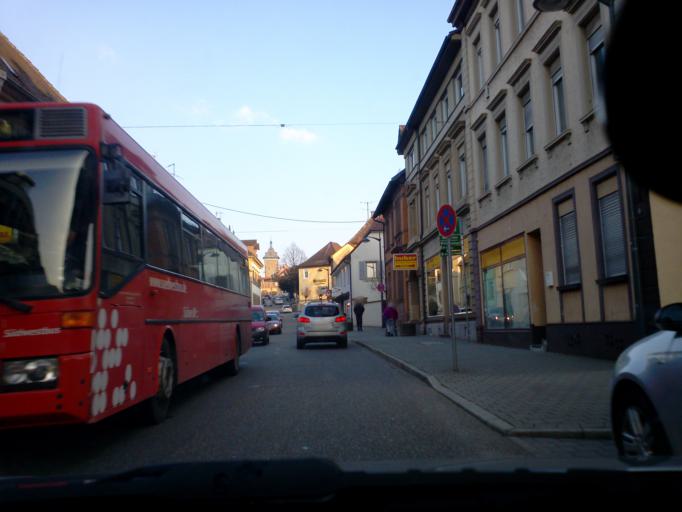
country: DE
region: Baden-Wuerttemberg
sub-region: Karlsruhe Region
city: Bretten
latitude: 49.0378
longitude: 8.7015
